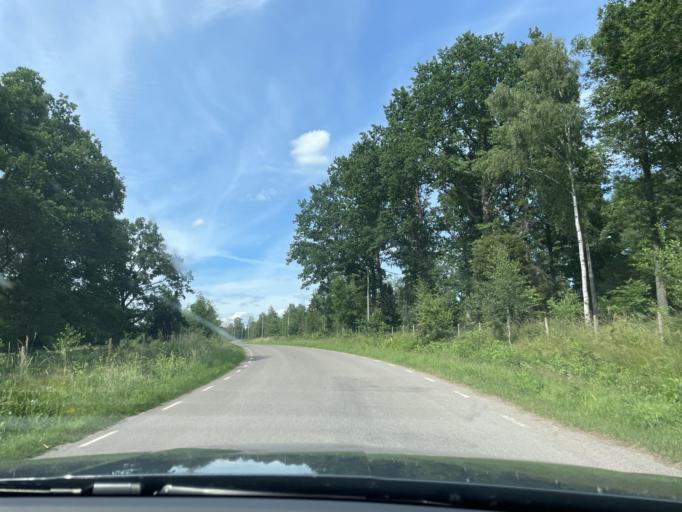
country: SE
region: Kalmar
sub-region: Vimmerby Kommun
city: Sodra Vi
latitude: 57.7689
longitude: 15.8144
